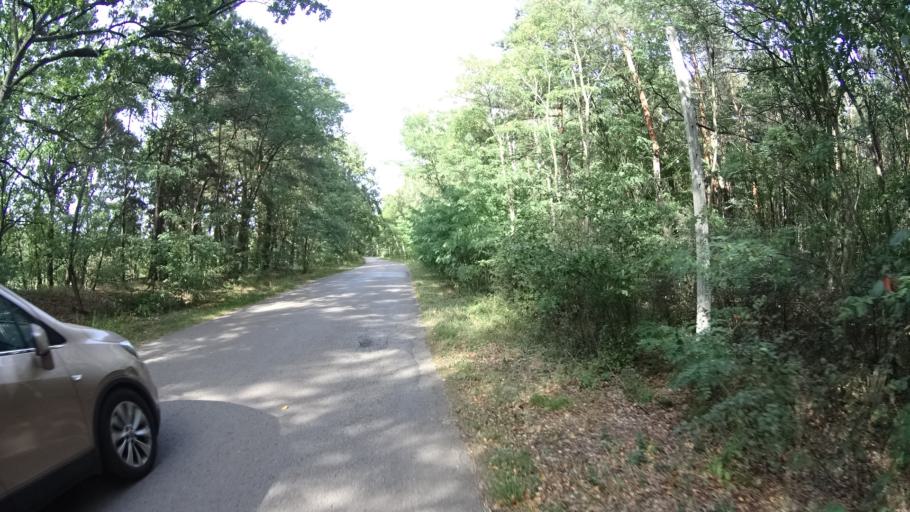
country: PL
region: Masovian Voivodeship
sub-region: Powiat legionowski
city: Serock
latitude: 52.4917
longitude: 21.0867
